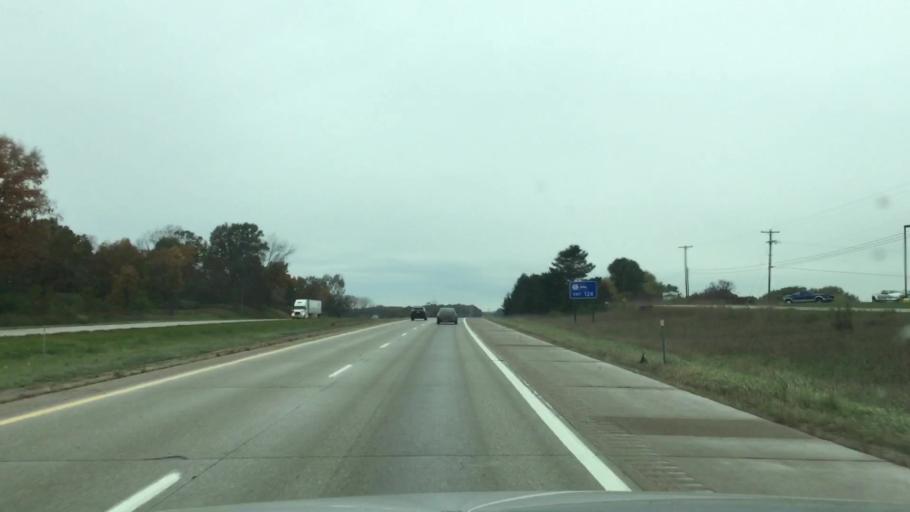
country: US
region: Michigan
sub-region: Calhoun County
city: Albion
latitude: 42.2622
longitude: -84.6990
